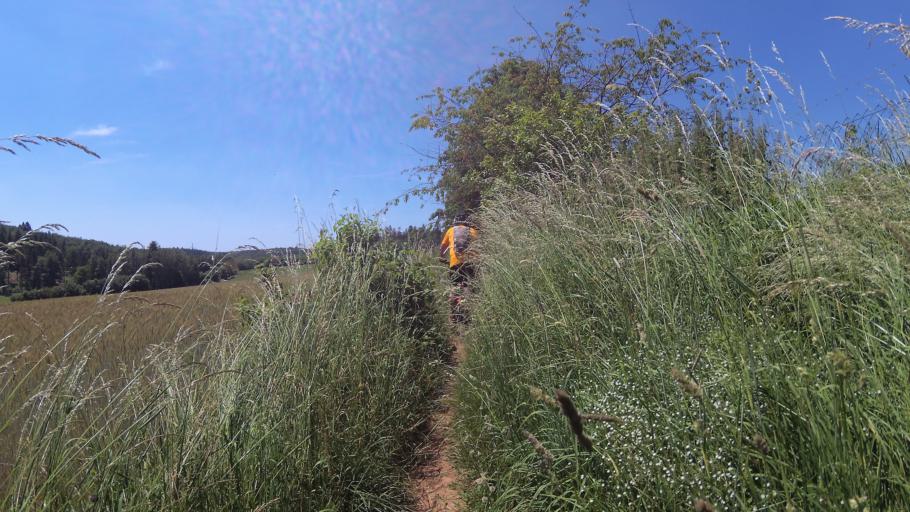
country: DE
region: Saarland
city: Saarwellingen
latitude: 49.3659
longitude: 6.8464
